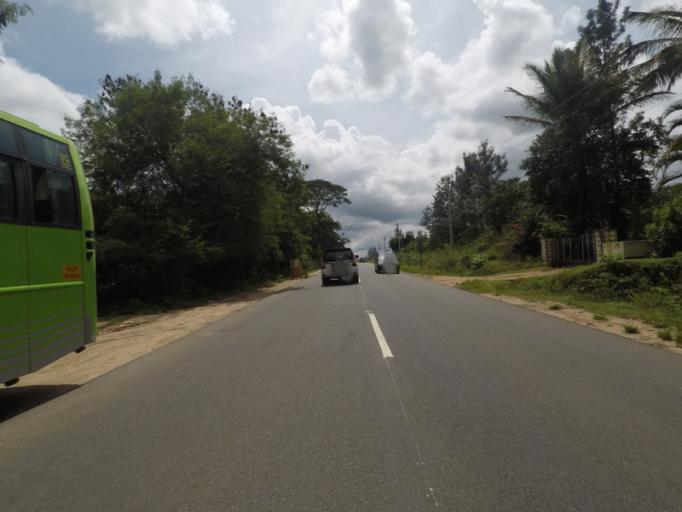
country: IN
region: Karnataka
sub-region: Kodagu
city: Kushalnagar
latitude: 12.4474
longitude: 75.9360
